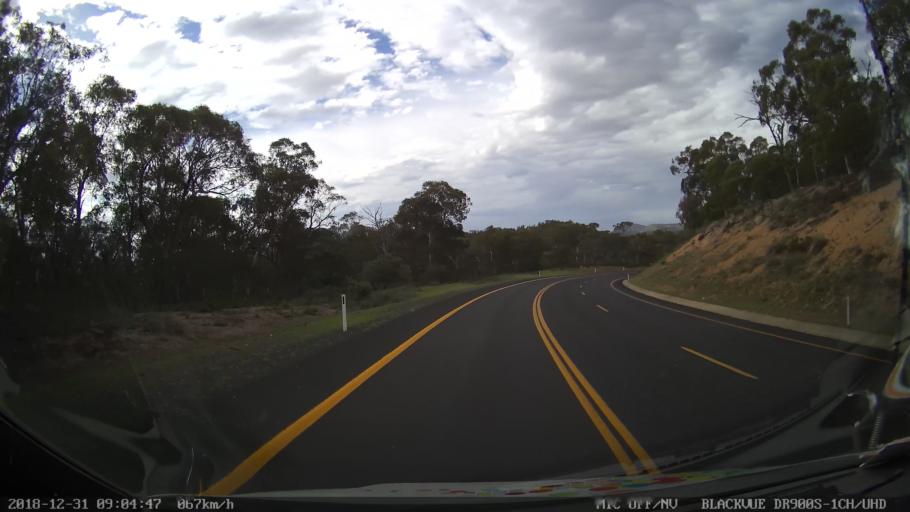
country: AU
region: New South Wales
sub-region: Snowy River
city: Jindabyne
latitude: -36.3570
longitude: 148.5896
